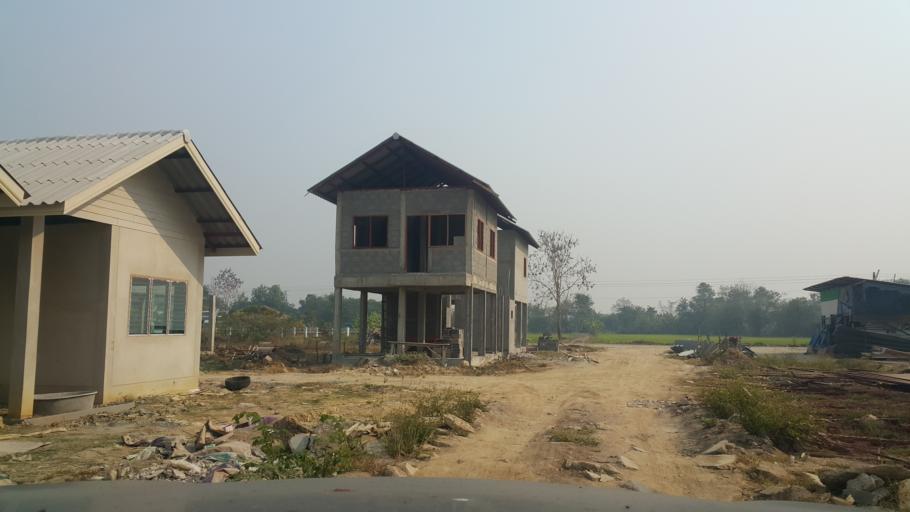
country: TH
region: Chiang Mai
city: San Kamphaeng
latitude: 18.7667
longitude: 99.0983
